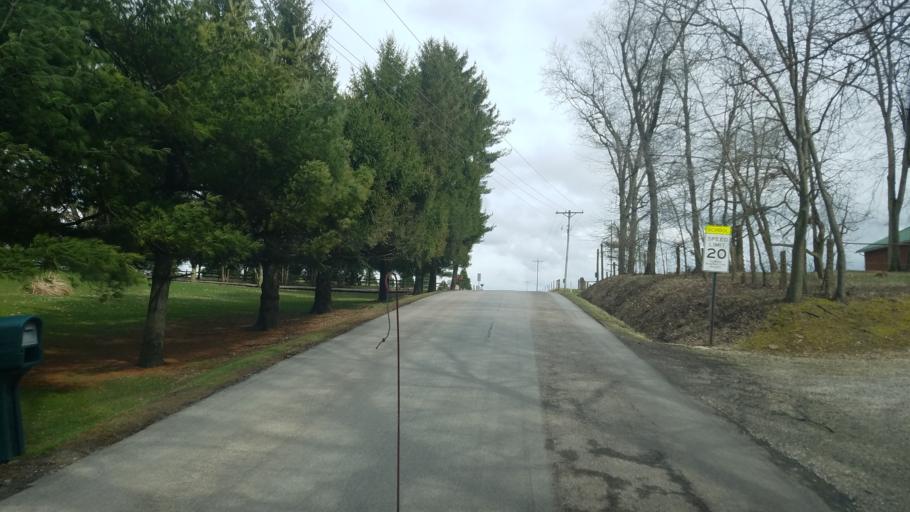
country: US
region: Ohio
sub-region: Wayne County
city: Apple Creek
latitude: 40.7263
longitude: -81.8341
